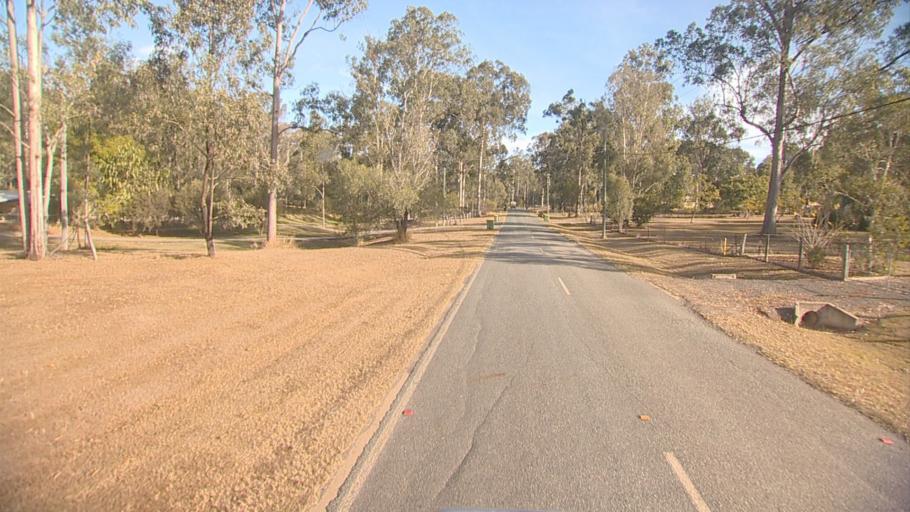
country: AU
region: Queensland
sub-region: Logan
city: Cedar Vale
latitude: -27.8776
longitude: 153.0017
